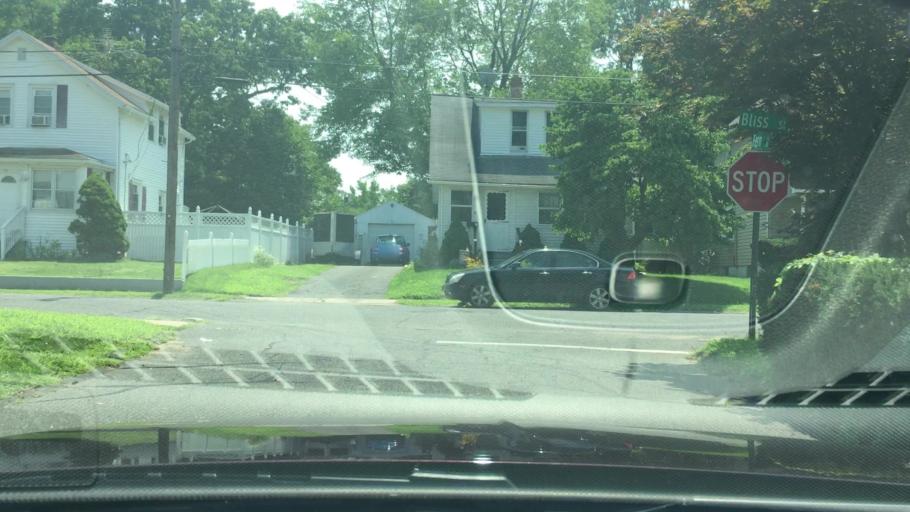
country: US
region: Connecticut
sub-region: Hartford County
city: East Hartford
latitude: 41.7829
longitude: -72.6055
